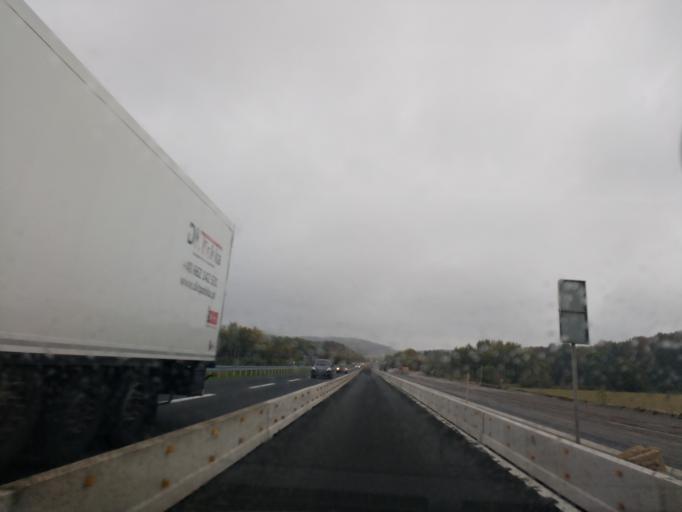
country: DE
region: Lower Saxony
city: Hilter
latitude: 52.1728
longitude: 8.1544
